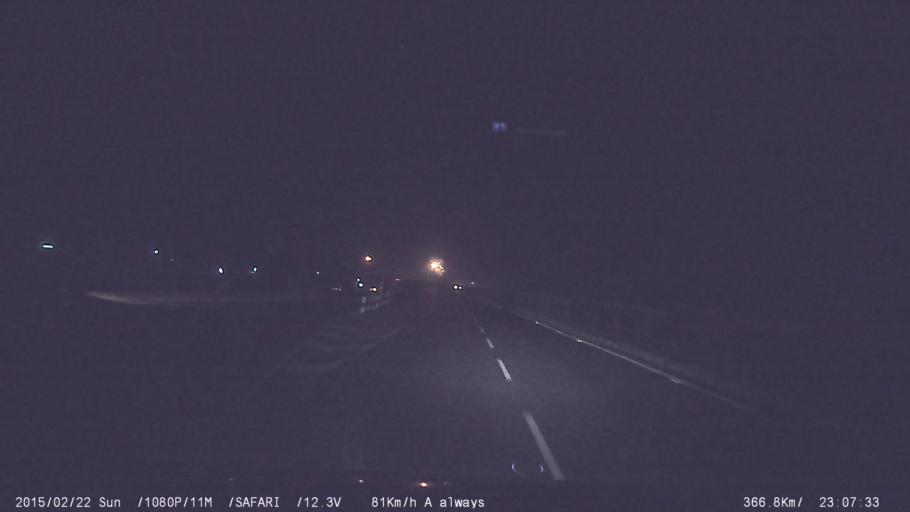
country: IN
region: Tamil Nadu
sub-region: Namakkal
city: Rasipuram
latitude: 11.4410
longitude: 78.1579
